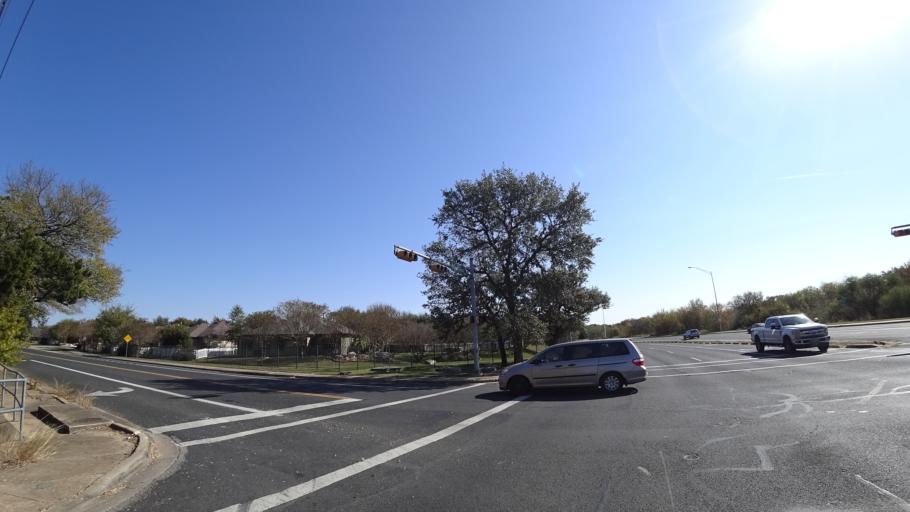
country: US
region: Texas
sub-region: Travis County
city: Shady Hollow
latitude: 30.2251
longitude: -97.8550
